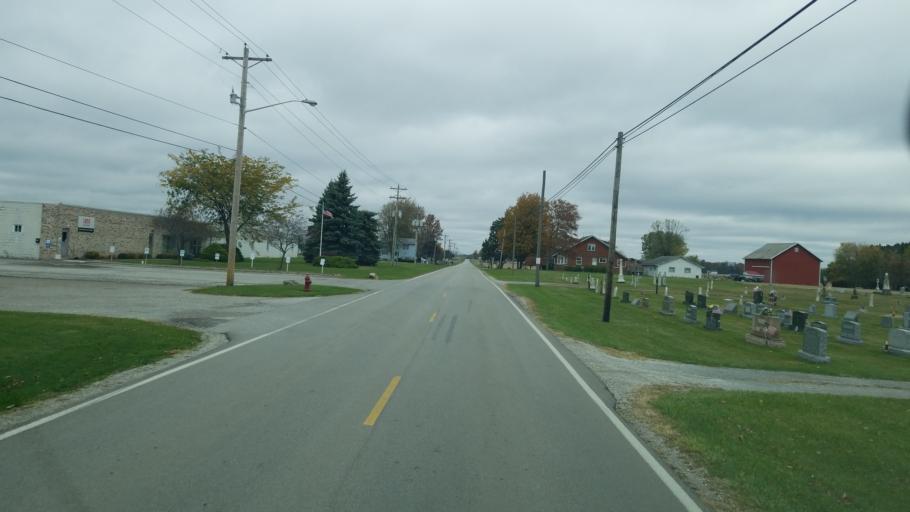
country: US
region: Ohio
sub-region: Huron County
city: Willard
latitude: 40.9674
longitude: -82.8535
